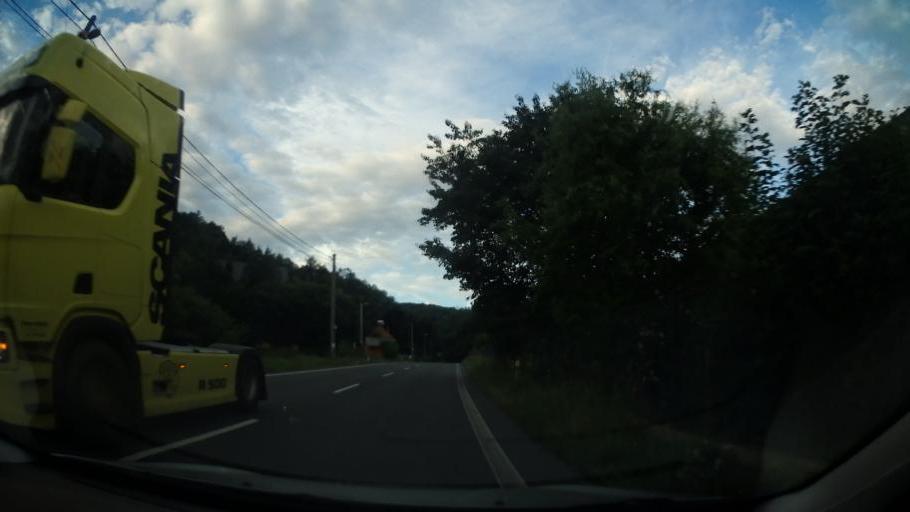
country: CZ
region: Olomoucky
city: Paseka
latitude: 49.8363
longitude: 17.2126
